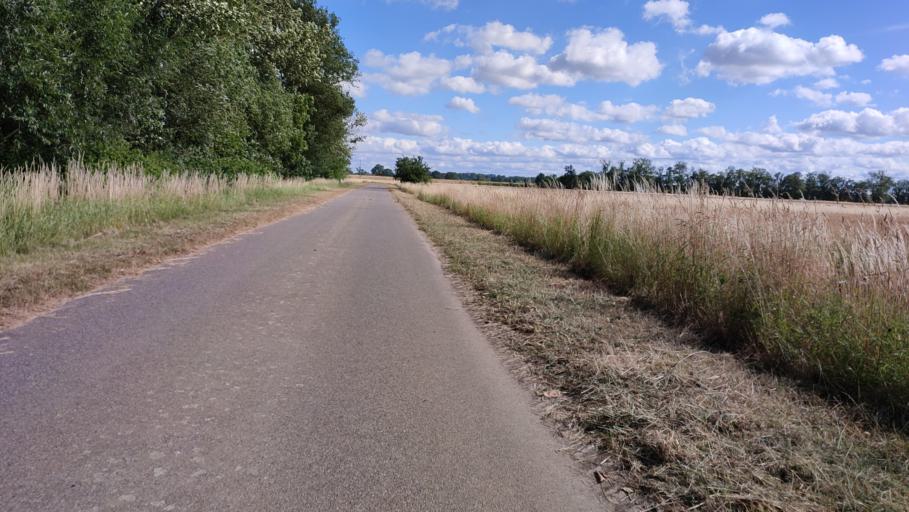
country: DE
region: Lower Saxony
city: Damnatz
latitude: 53.1816
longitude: 11.1468
